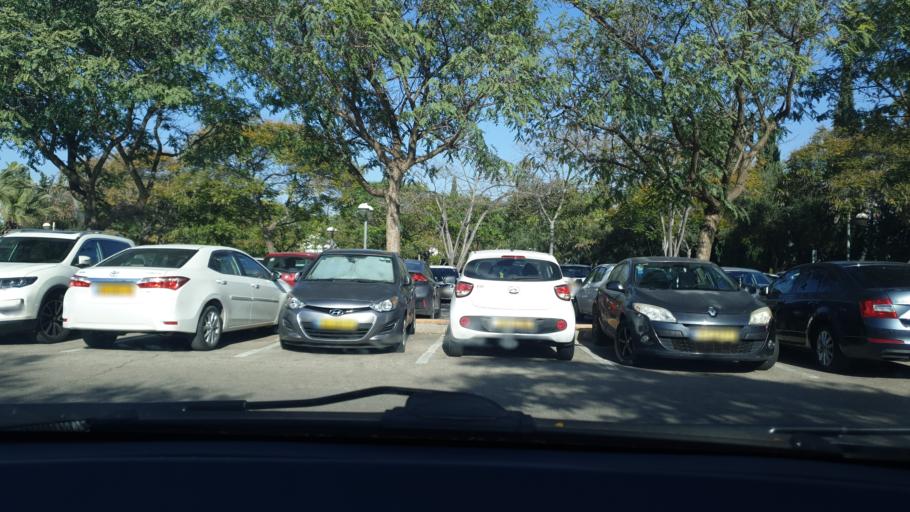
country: IL
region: Central District
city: Kefar Habad
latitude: 31.9660
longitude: 34.8418
